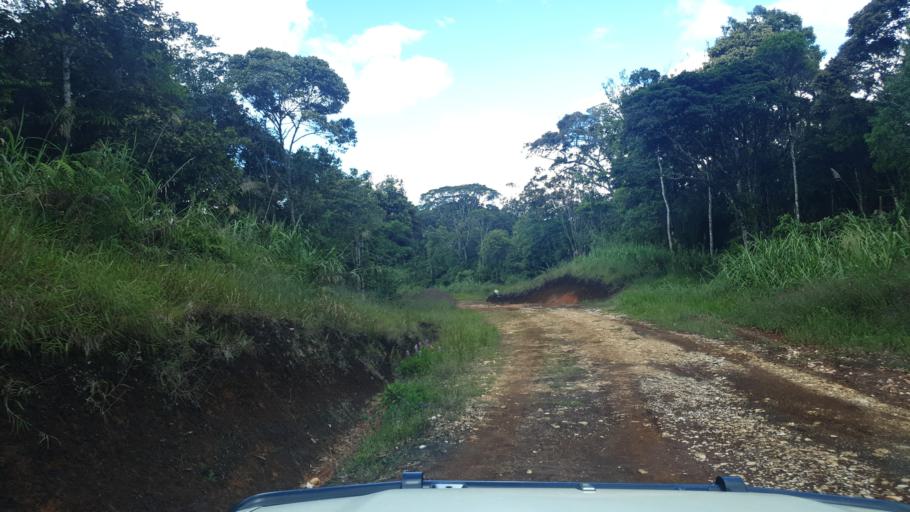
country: PG
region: Eastern Highlands
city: Goroka
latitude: -6.2791
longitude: 145.1946
